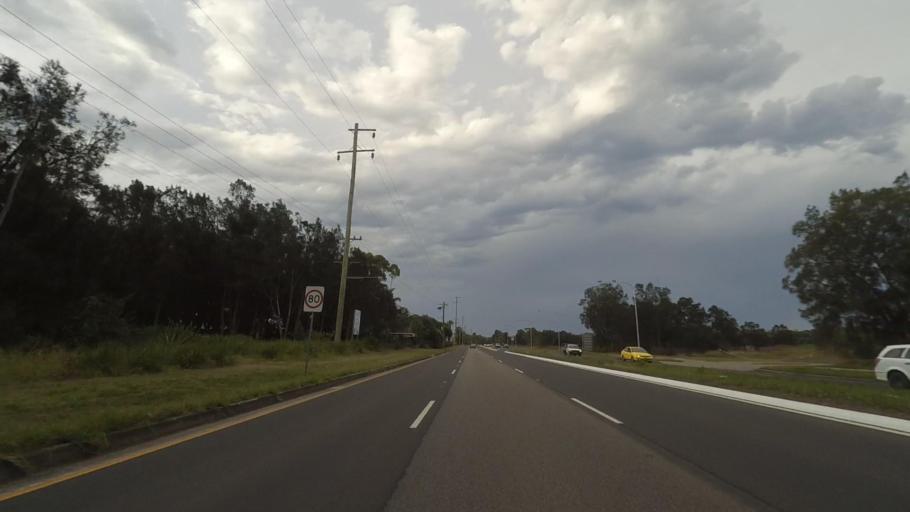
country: AU
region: New South Wales
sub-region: Shellharbour
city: Lake Illawarra
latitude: -34.5200
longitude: 150.8716
